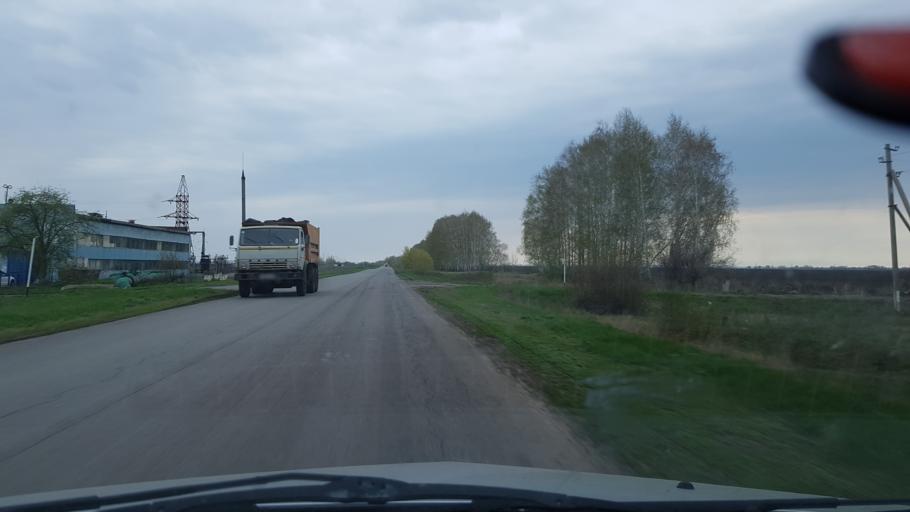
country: RU
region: Samara
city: Podstepki
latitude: 53.6661
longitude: 49.1639
